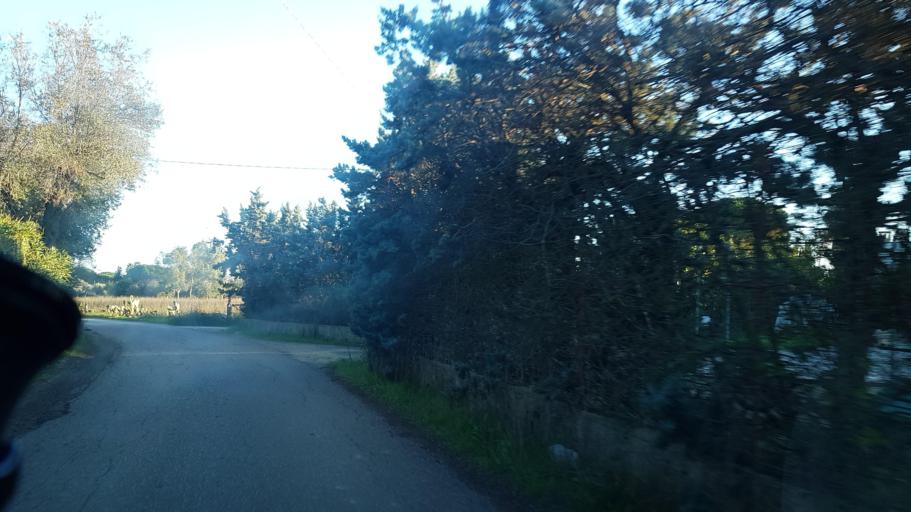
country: IT
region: Apulia
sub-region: Provincia di Brindisi
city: Mesagne
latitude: 40.5642
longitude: 17.7787
